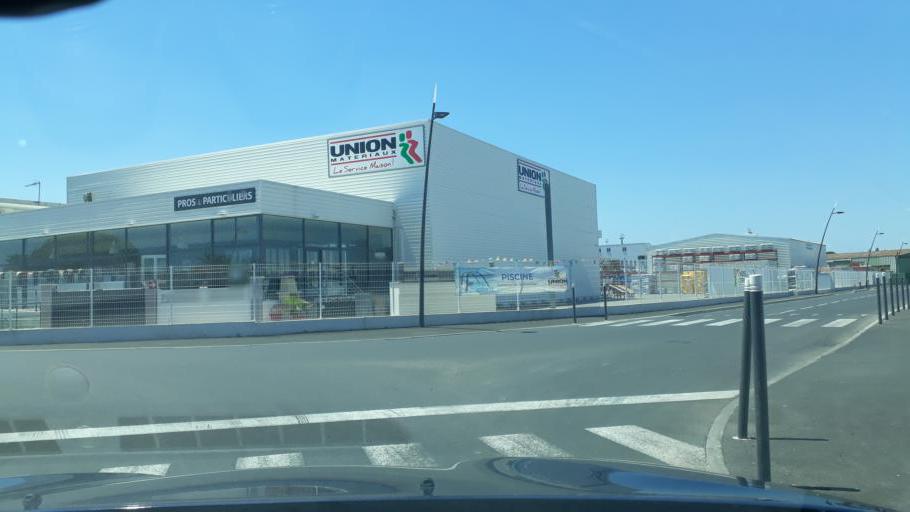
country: FR
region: Languedoc-Roussillon
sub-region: Departement de l'Herault
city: Agde
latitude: 43.3098
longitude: 3.4923
